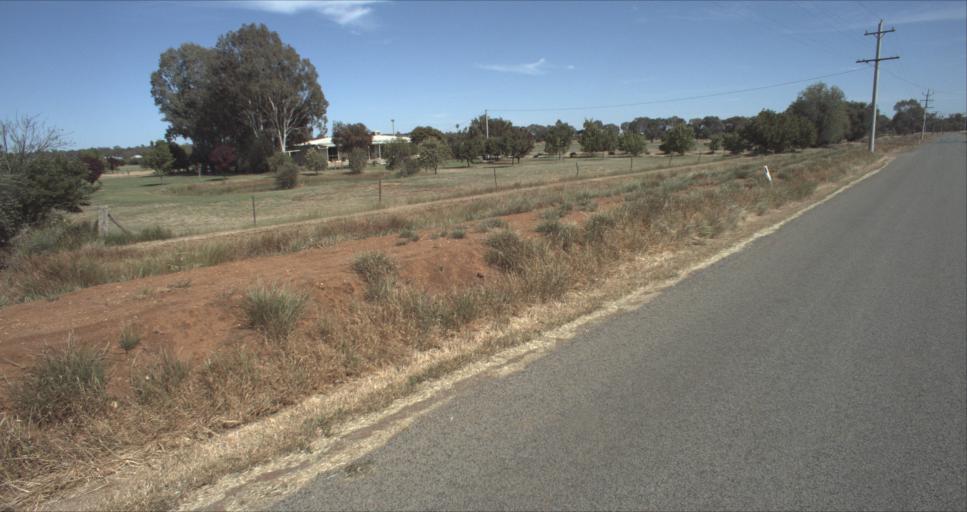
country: AU
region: New South Wales
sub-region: Leeton
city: Leeton
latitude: -34.5813
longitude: 146.4695
